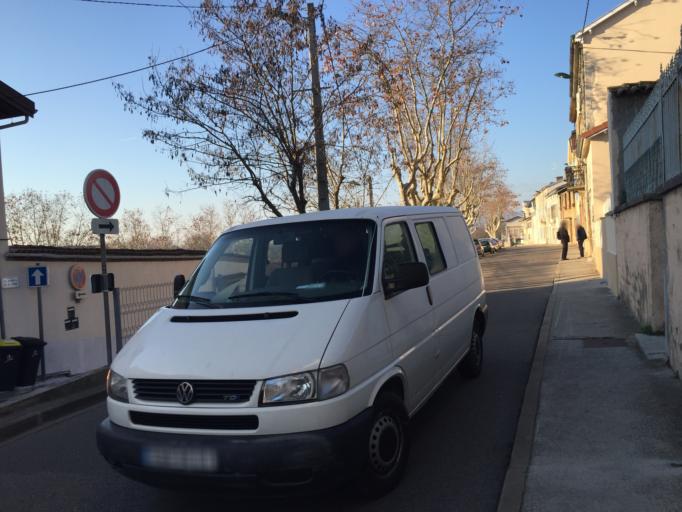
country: FR
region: Rhone-Alpes
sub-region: Departement de l'Ain
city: Miribel
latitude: 45.8230
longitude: 4.9552
